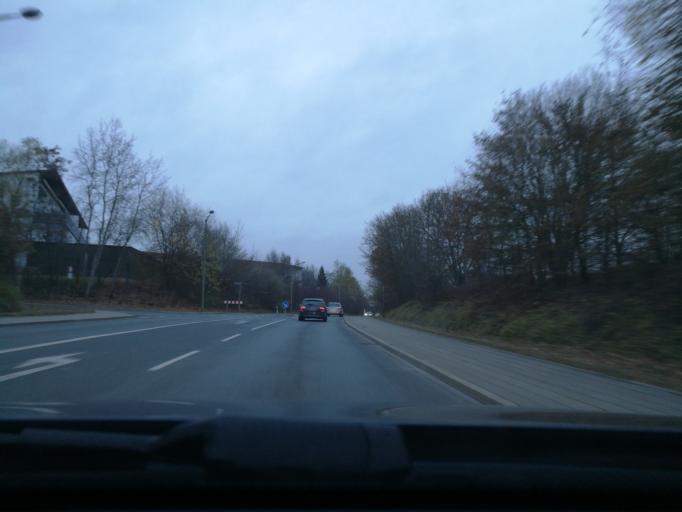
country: DE
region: Bavaria
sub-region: Regierungsbezirk Mittelfranken
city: Furth
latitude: 49.4720
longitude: 10.9651
